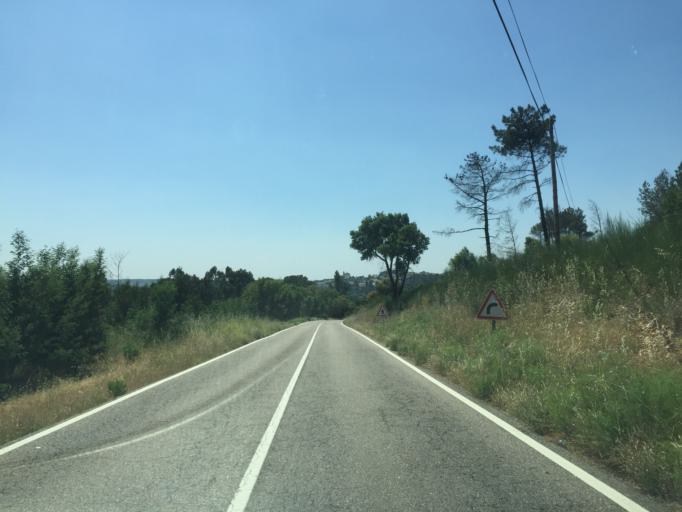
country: PT
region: Santarem
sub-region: Constancia
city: Constancia
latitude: 39.4811
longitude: -8.3172
